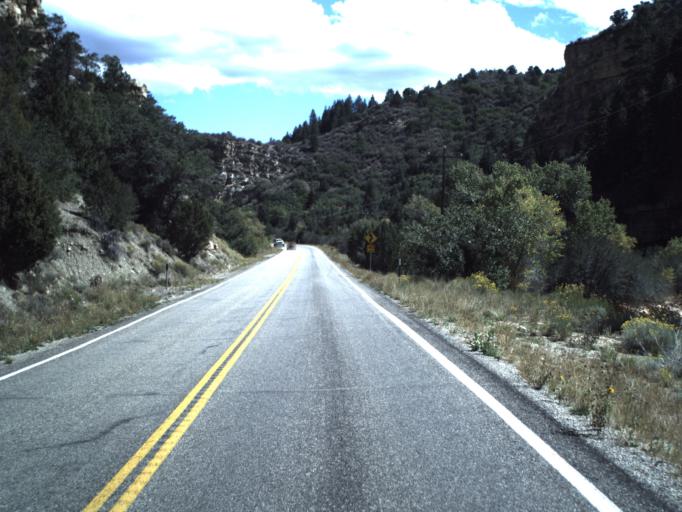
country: US
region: Utah
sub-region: Iron County
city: Cedar City
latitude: 37.6444
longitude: -112.9660
